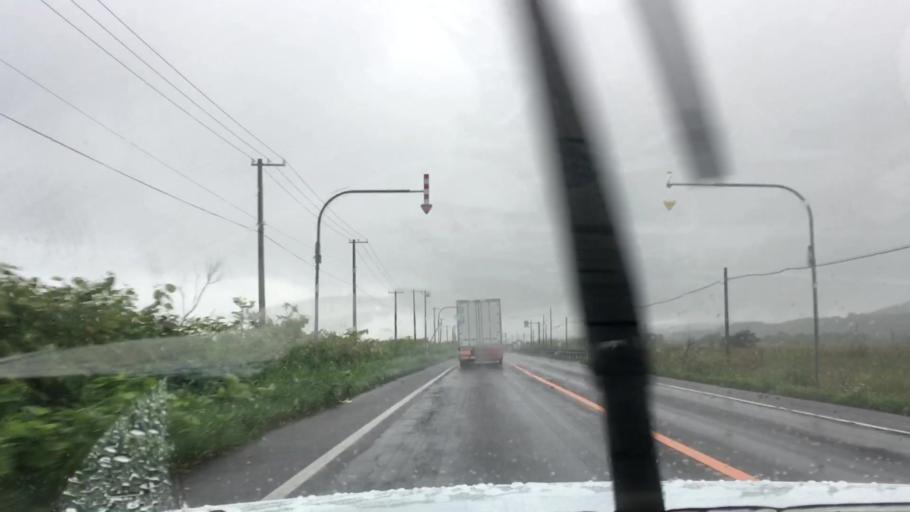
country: JP
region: Hokkaido
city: Niseko Town
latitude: 42.4269
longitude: 140.3164
